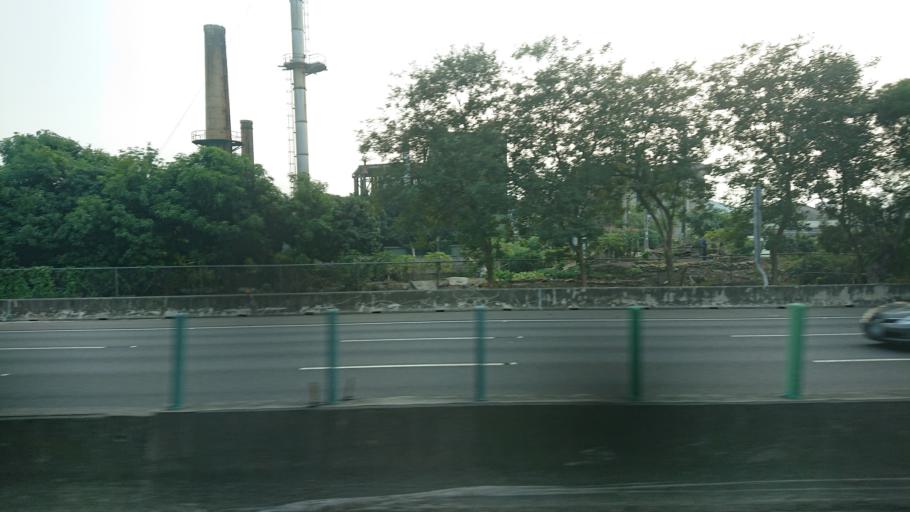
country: TW
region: Taiwan
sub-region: Changhua
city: Chang-hua
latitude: 24.1162
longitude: 120.5923
